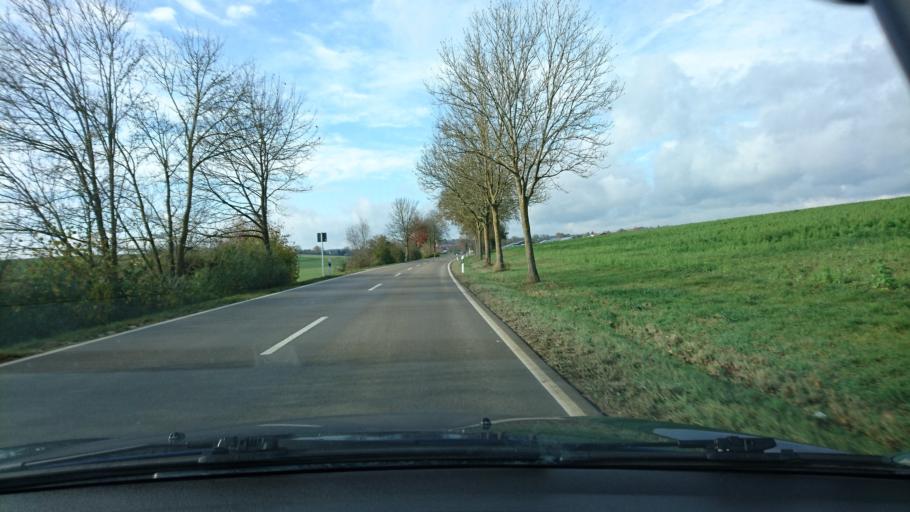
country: DE
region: Bavaria
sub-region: Swabia
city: Amerdingen
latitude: 48.7255
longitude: 10.5015
